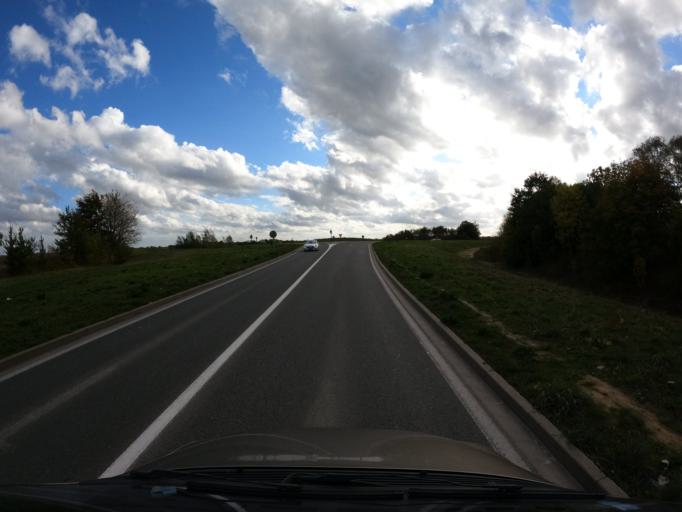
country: FR
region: Ile-de-France
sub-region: Departement de Seine-et-Marne
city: Coupvray
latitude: 48.8842
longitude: 2.8067
